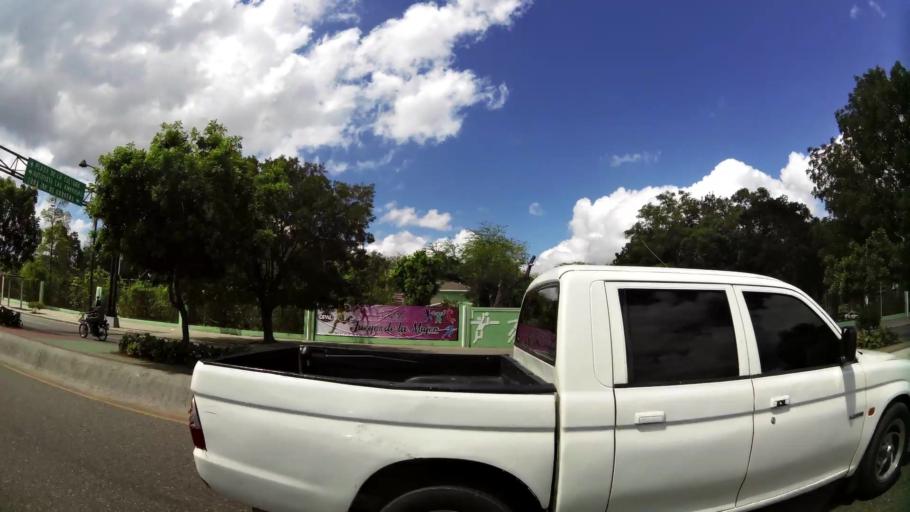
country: DO
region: Nacional
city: San Carlos
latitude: 18.4779
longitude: -69.9138
